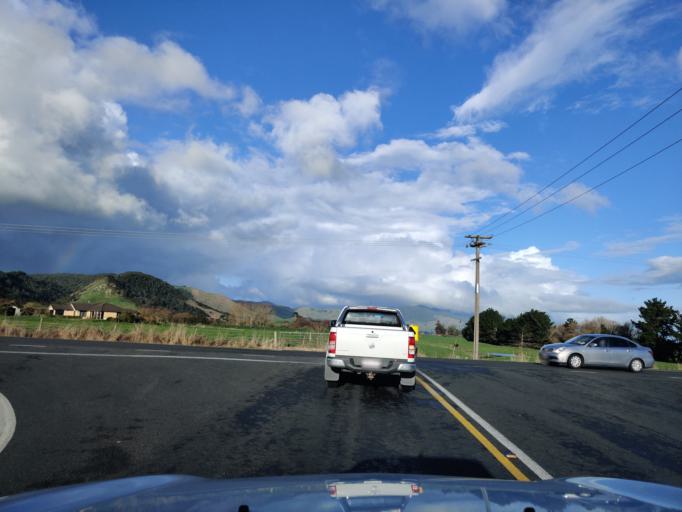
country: NZ
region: Waikato
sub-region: Hauraki District
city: Paeroa
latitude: -37.4425
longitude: 175.6319
